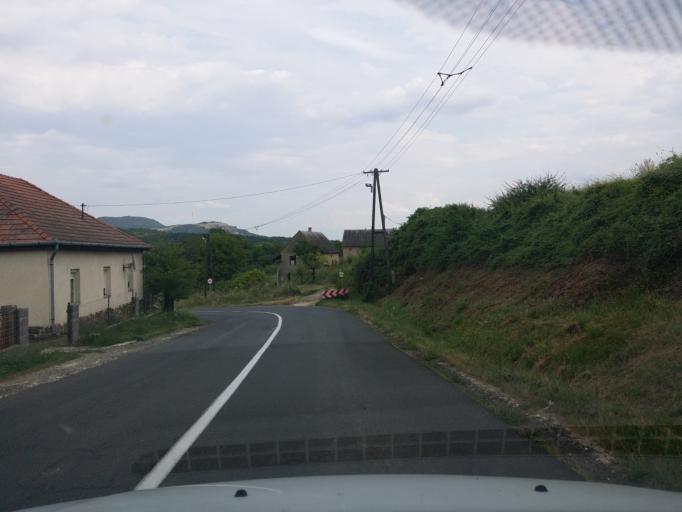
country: HU
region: Nograd
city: Bercel
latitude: 47.9145
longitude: 19.3724
